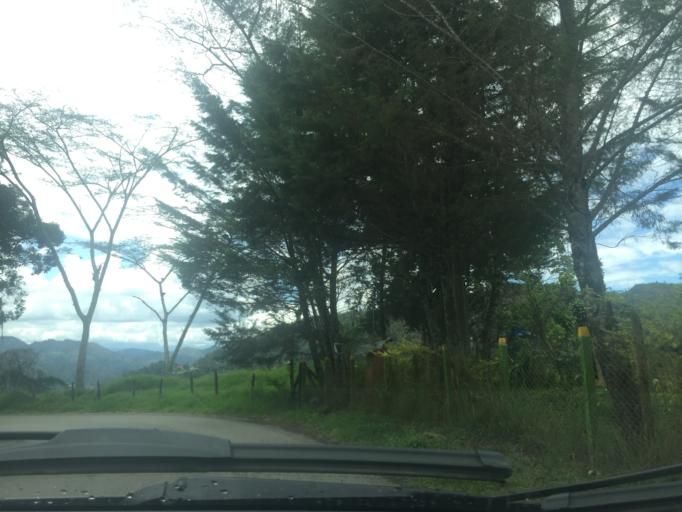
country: CO
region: Cundinamarca
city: San Francisco
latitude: 4.9970
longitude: -74.2837
